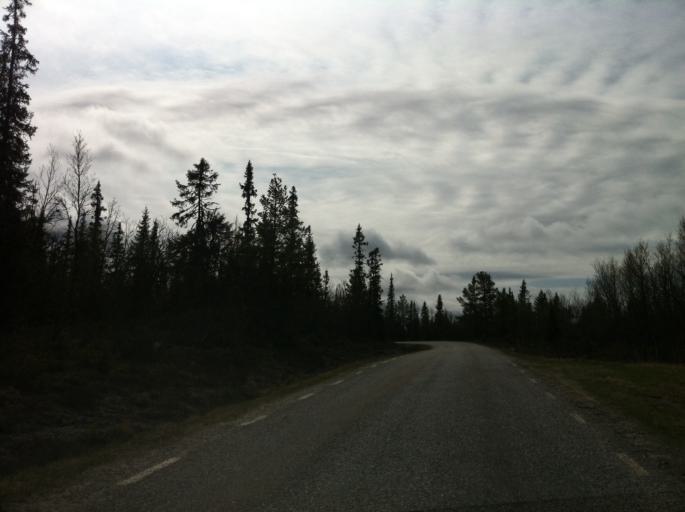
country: NO
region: Hedmark
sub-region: Engerdal
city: Engerdal
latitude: 62.3096
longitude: 12.8085
